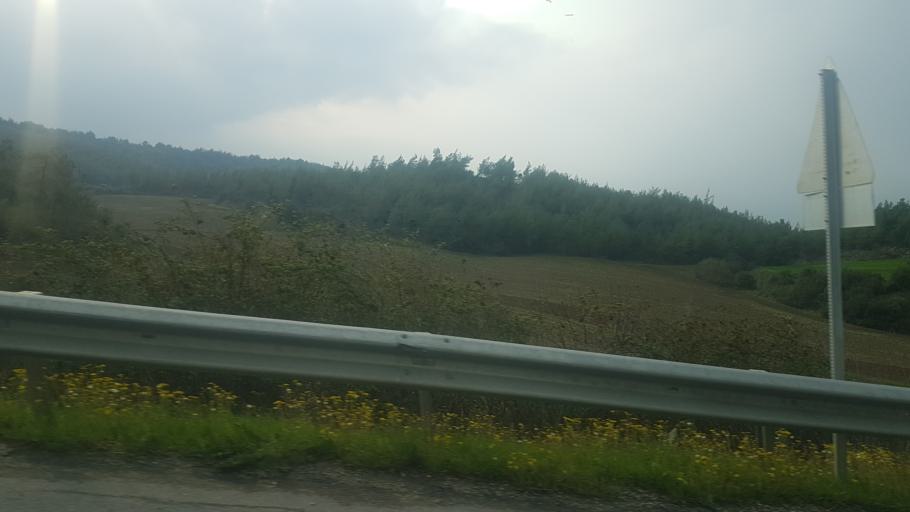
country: TR
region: Mersin
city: Yenice
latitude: 37.0810
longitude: 35.1733
